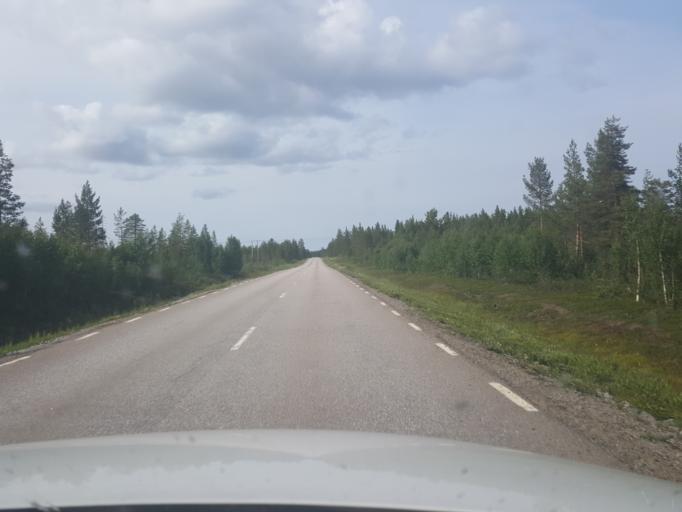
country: SE
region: Norrbotten
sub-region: Arjeplogs Kommun
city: Arjeplog
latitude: 65.6656
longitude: 18.0800
